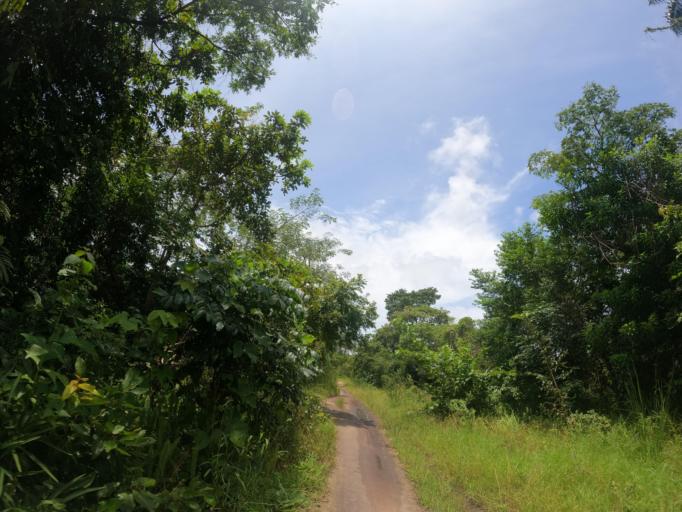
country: SL
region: Northern Province
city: Binkolo
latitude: 9.1437
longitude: -12.2426
